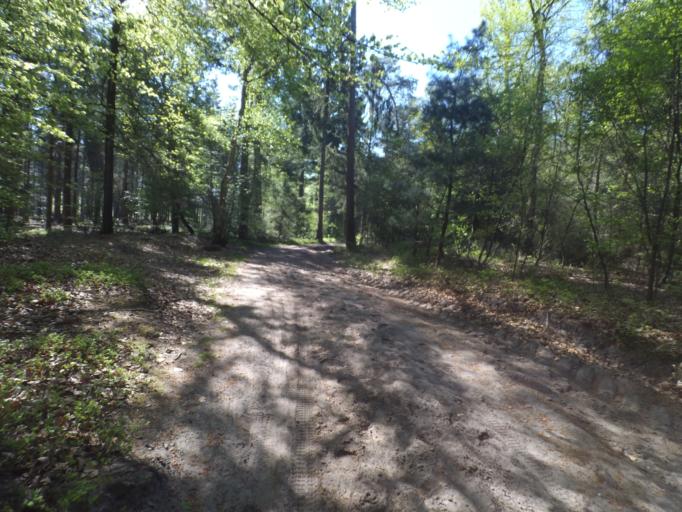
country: NL
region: Utrecht
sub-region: Gemeente Utrechtse Heuvelrug
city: Maarn
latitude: 52.0868
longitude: 5.3807
